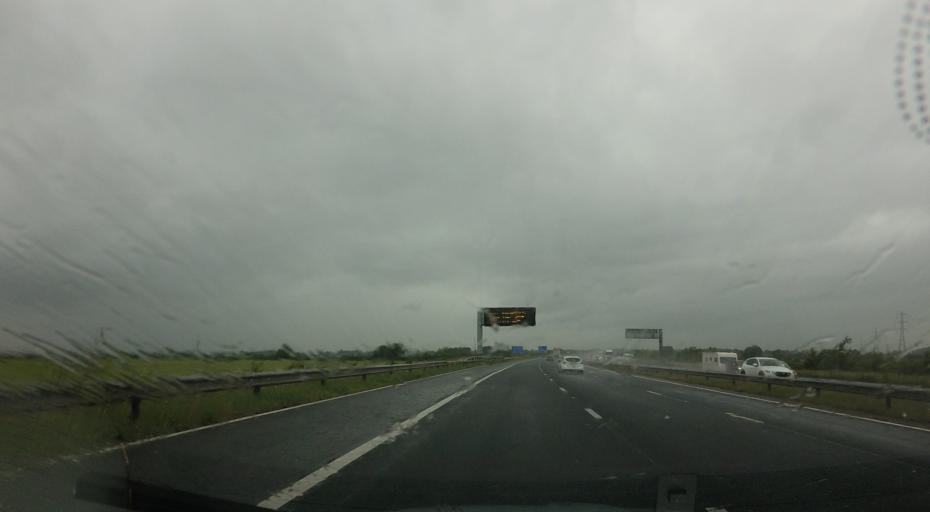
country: GB
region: Scotland
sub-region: Dumfries and Galloway
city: Gretna
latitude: 54.9854
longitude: -3.0350
